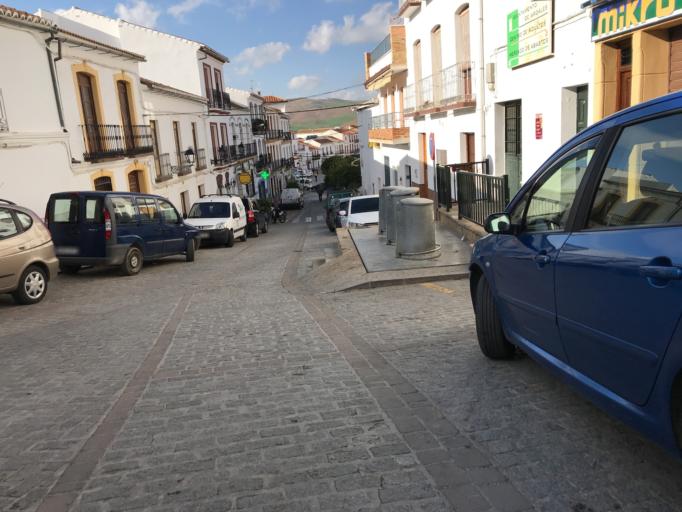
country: ES
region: Andalusia
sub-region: Provincia de Malaga
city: Ardales
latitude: 36.8777
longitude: -4.8464
